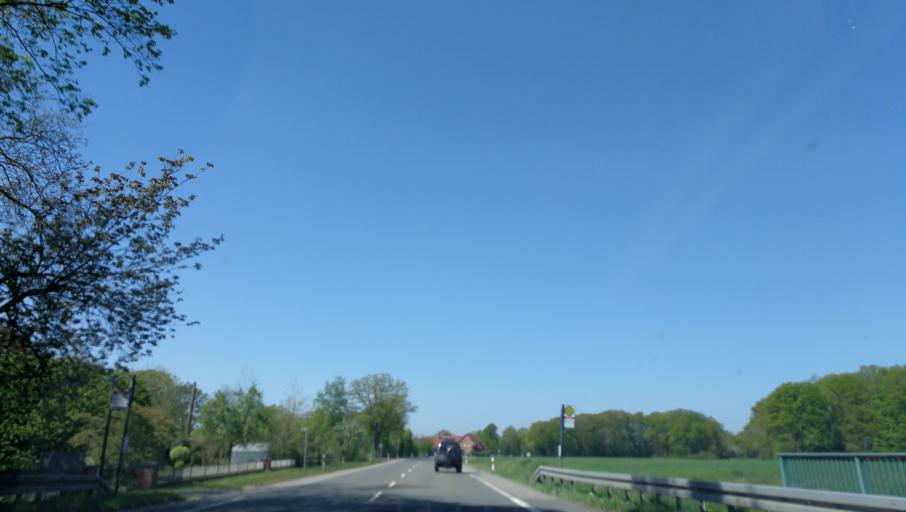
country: DE
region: North Rhine-Westphalia
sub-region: Regierungsbezirk Munster
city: Wettringen
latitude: 52.1862
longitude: 7.3323
